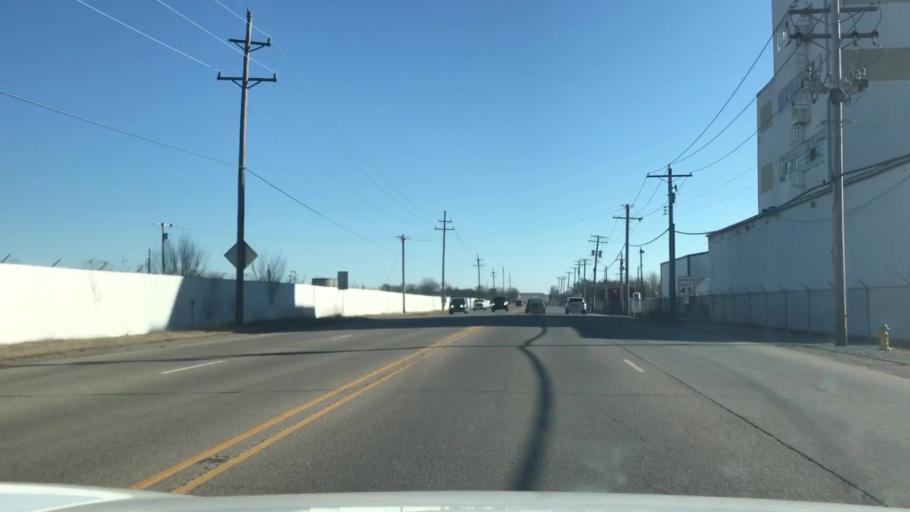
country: US
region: Illinois
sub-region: Saint Clair County
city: Alorton
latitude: 38.5990
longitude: -90.1268
